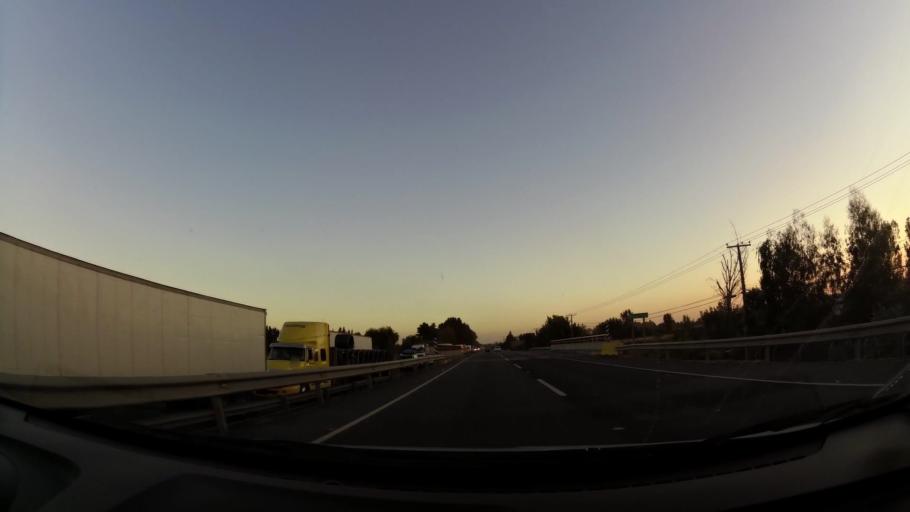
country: CL
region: Maule
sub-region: Provincia de Linares
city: Linares
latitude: -35.7486
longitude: -71.6739
